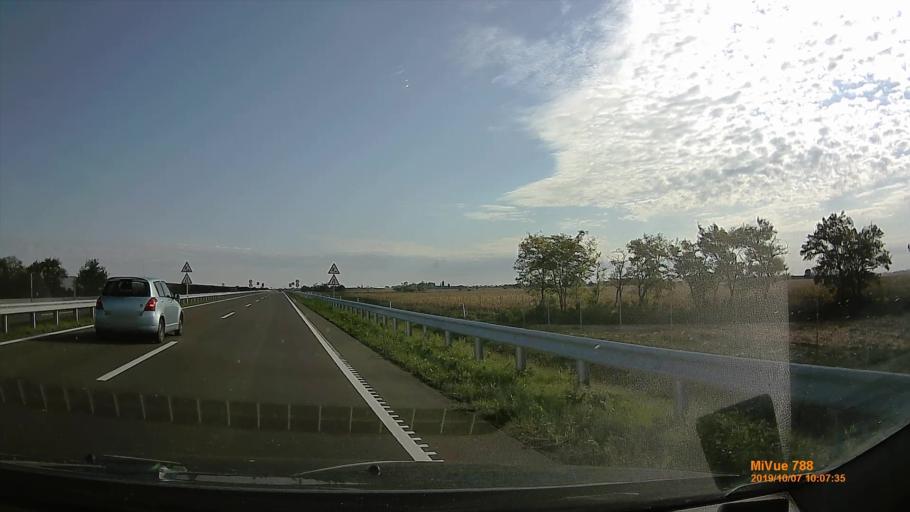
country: HU
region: Bekes
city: Kondoros
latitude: 46.7430
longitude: 20.8332
